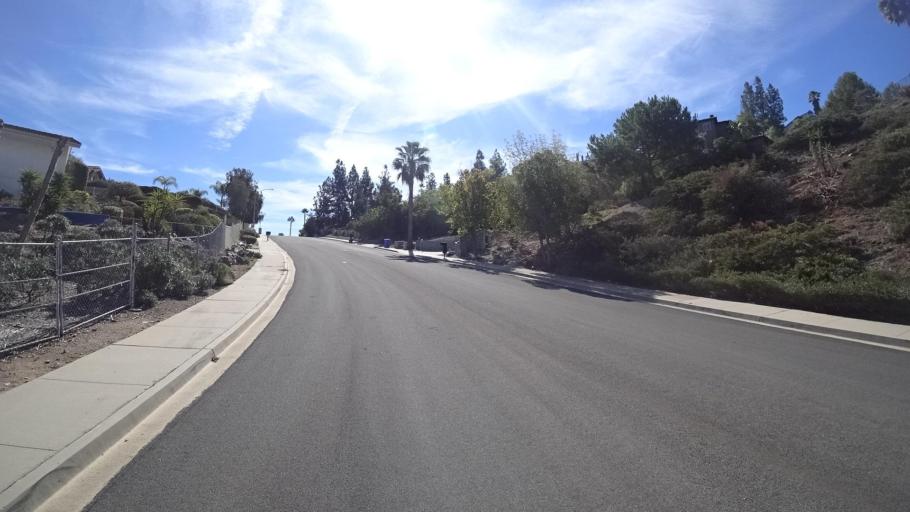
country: US
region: California
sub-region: San Diego County
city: Casa de Oro-Mount Helix
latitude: 32.7583
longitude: -116.9509
